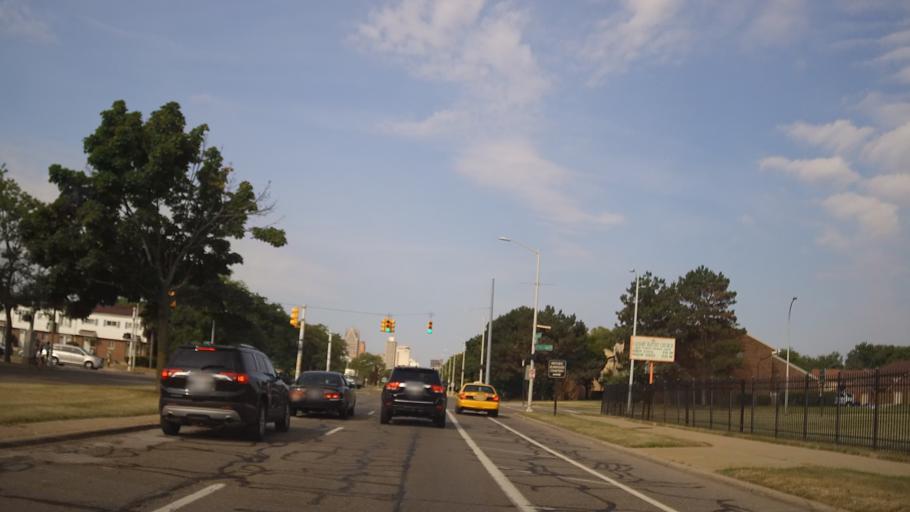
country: US
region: Michigan
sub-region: Wayne County
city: Detroit
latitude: 42.3445
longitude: -83.0178
